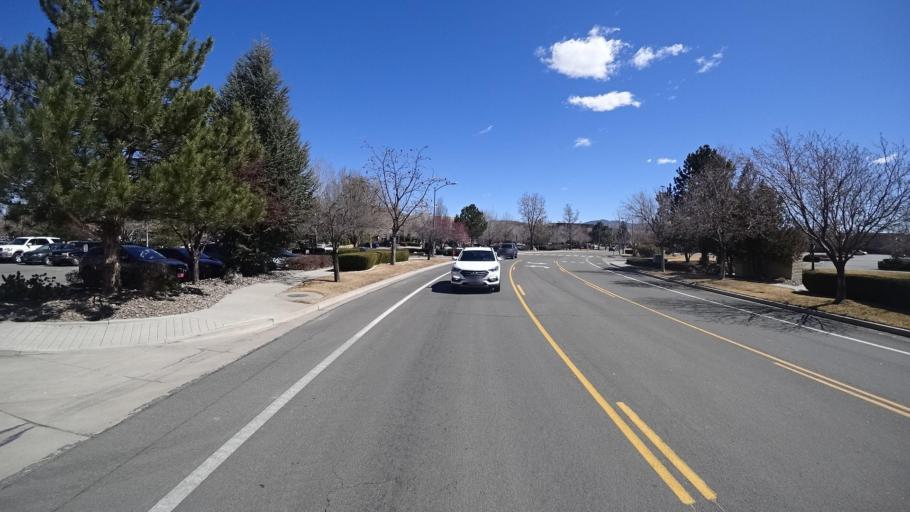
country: US
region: Nevada
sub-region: Washoe County
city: Reno
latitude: 39.4659
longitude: -119.7793
